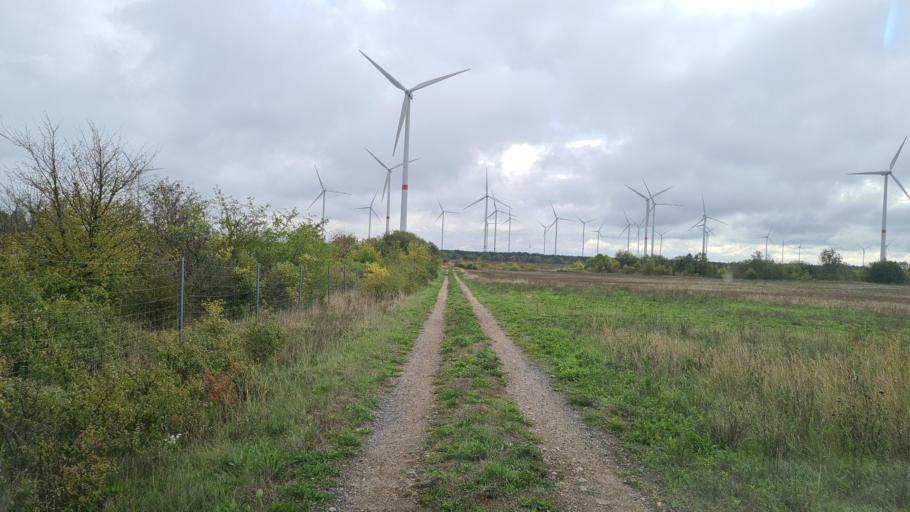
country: DE
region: Brandenburg
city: Sallgast
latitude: 51.5573
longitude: 13.8279
